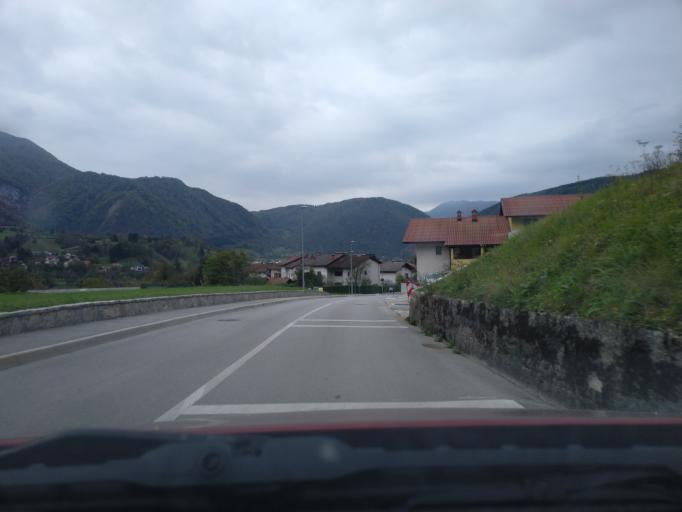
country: SI
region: Tolmin
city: Tolmin
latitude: 46.1910
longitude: 13.7300
